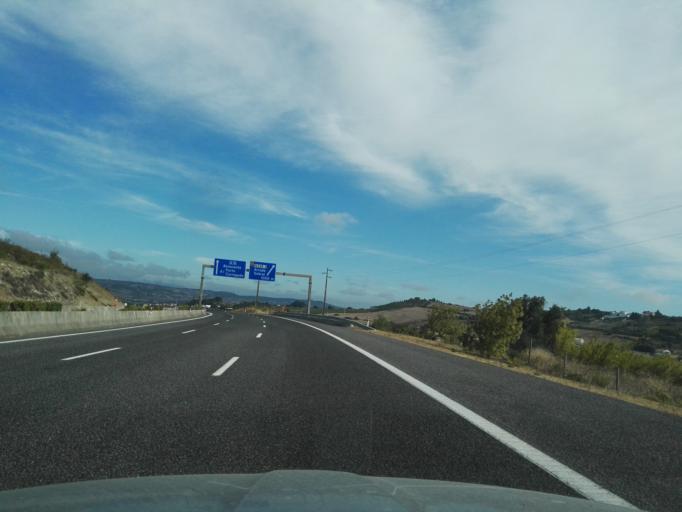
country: PT
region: Lisbon
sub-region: Arruda Dos Vinhos
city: Arruda dos Vinhos
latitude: 38.9560
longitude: -9.0621
